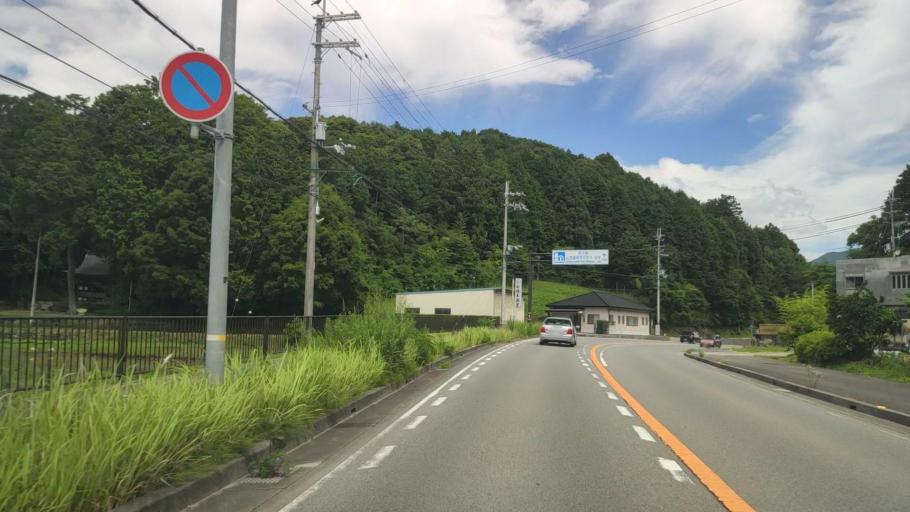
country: JP
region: Hyogo
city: Nishiwaki
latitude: 35.0541
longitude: 134.9173
